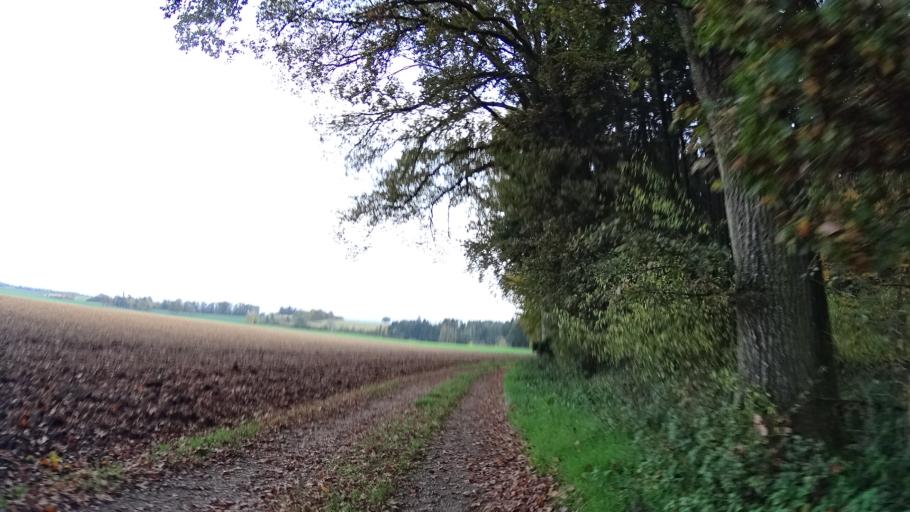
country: DE
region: Bavaria
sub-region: Upper Bavaria
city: Hitzhofen
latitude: 48.8448
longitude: 11.3019
